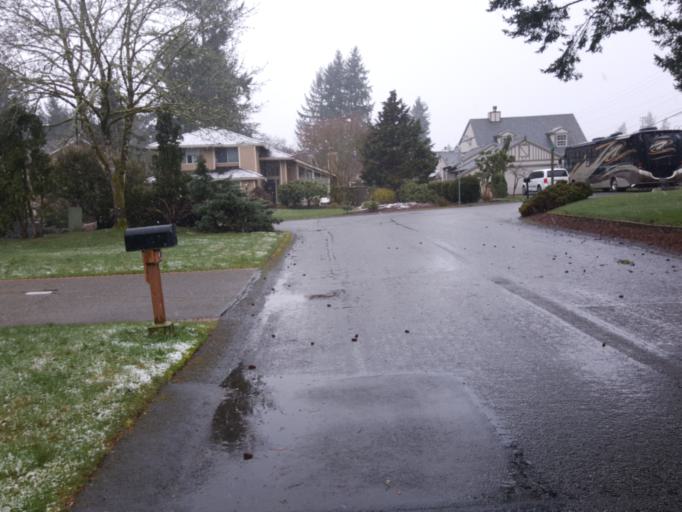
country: US
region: Washington
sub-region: Pierce County
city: Lakewood
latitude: 47.1986
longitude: -122.5414
